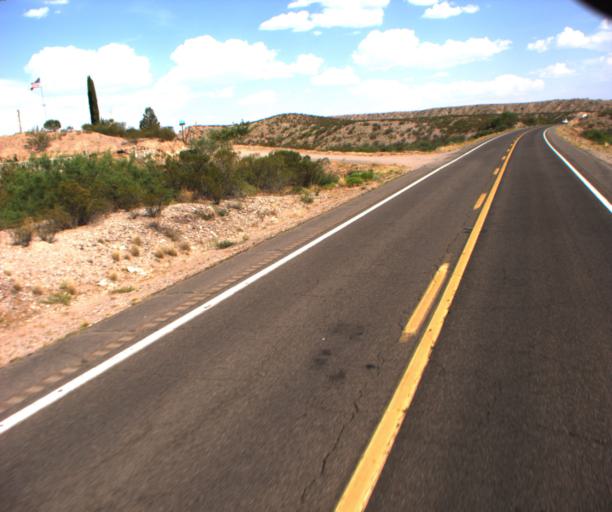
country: US
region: Arizona
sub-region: Greenlee County
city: Clifton
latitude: 32.8132
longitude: -109.1696
